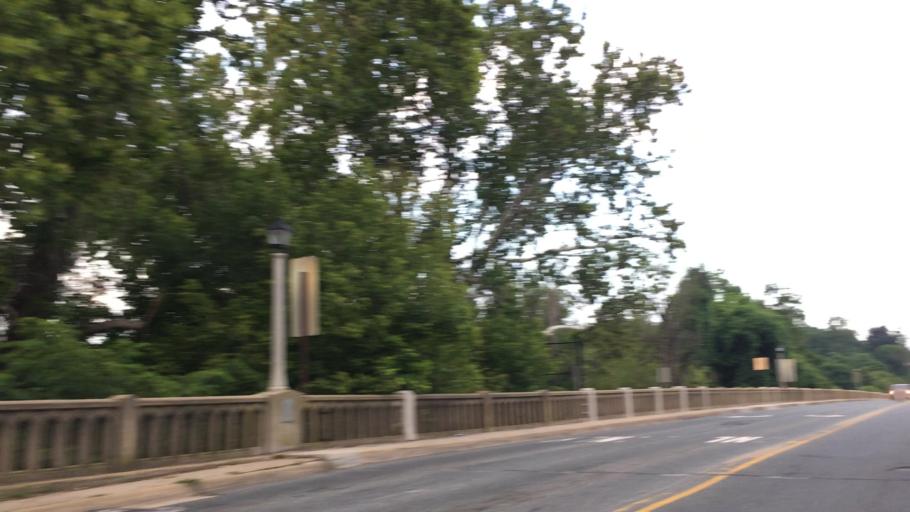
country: US
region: Virginia
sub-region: City of Fredericksburg
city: Fredericksburg
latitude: 38.3041
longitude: -77.4585
